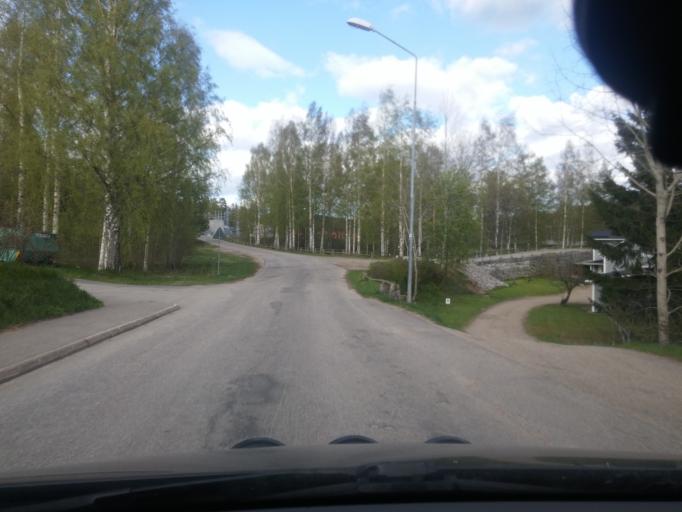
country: SE
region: Gaevleborg
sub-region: Bollnas Kommun
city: Arbra
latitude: 61.4758
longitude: 16.3825
